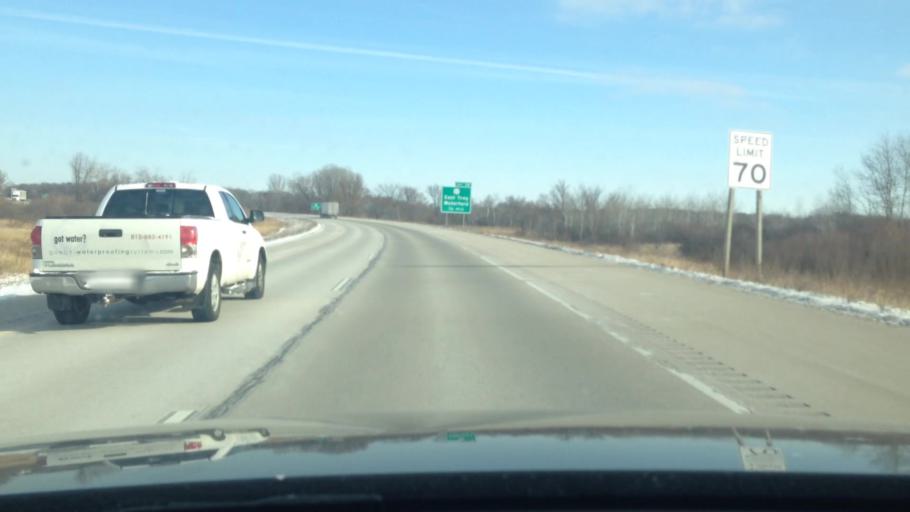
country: US
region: Wisconsin
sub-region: Walworth County
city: East Troy
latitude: 42.7779
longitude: -88.3940
